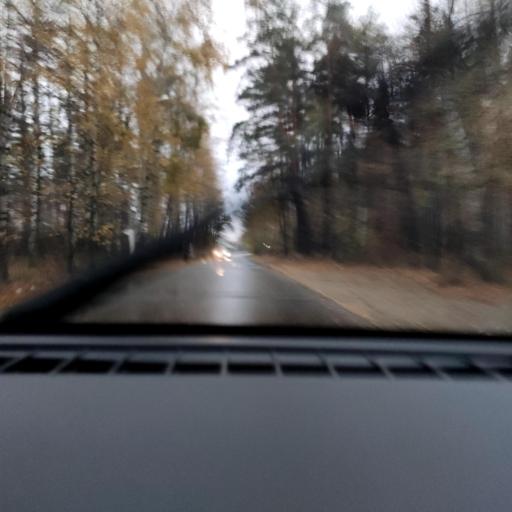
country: RU
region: Voronezj
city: Somovo
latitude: 51.6948
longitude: 39.3143
